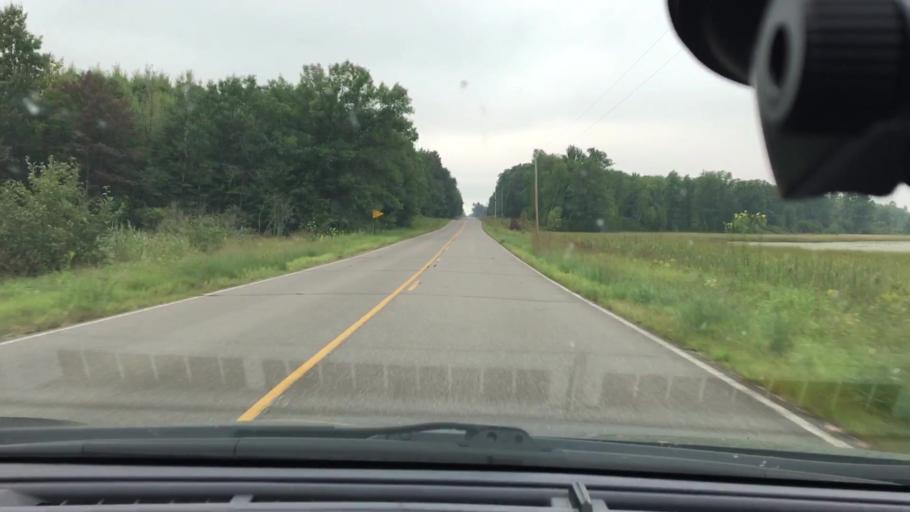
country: US
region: Minnesota
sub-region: Crow Wing County
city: Cross Lake
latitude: 46.6534
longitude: -94.0094
